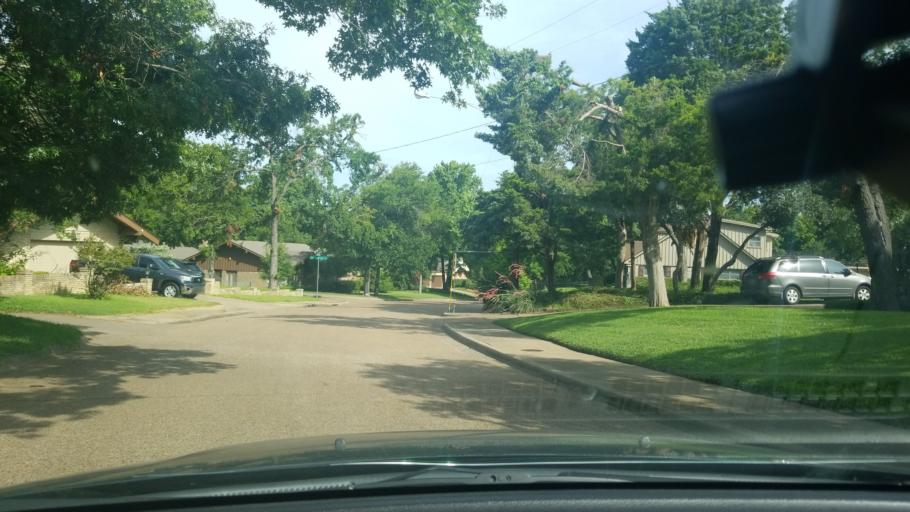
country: US
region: Texas
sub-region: Dallas County
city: Highland Park
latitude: 32.7984
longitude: -96.7010
